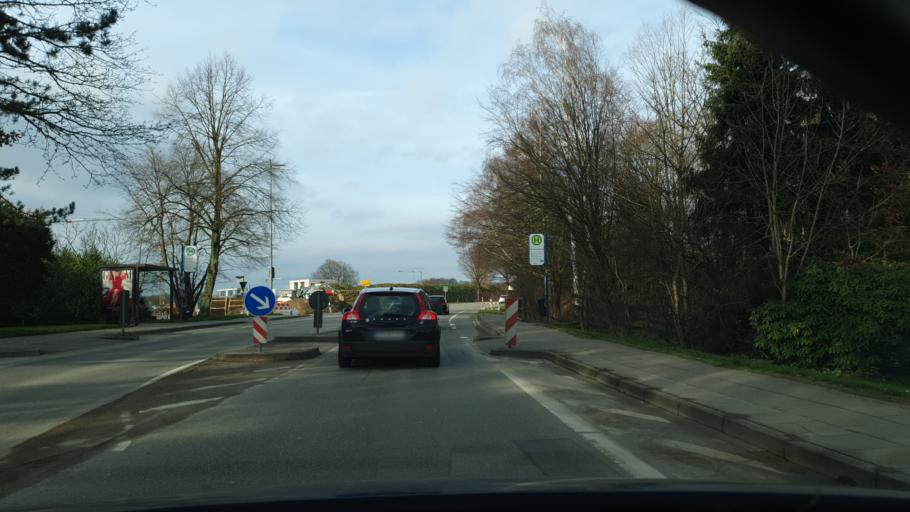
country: DE
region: North Rhine-Westphalia
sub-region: Regierungsbezirk Detmold
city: Bielefeld
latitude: 52.0735
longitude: 8.5148
